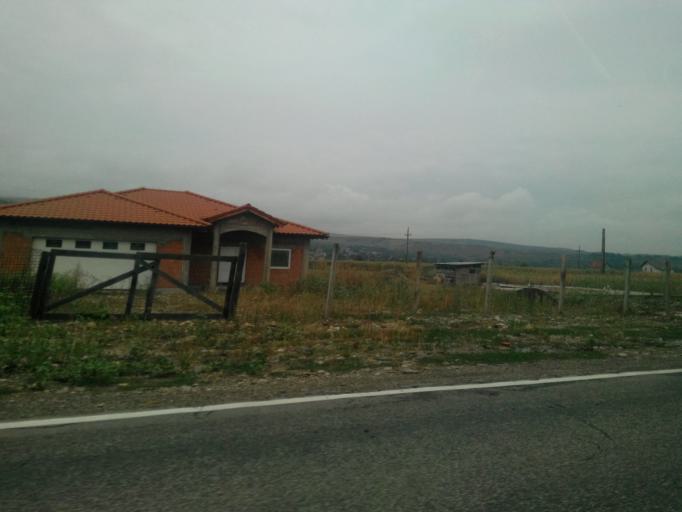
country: RO
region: Cluj
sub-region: Comuna Mihai Viteazu
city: Mihai Viteazu
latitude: 46.5320
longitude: 23.7118
